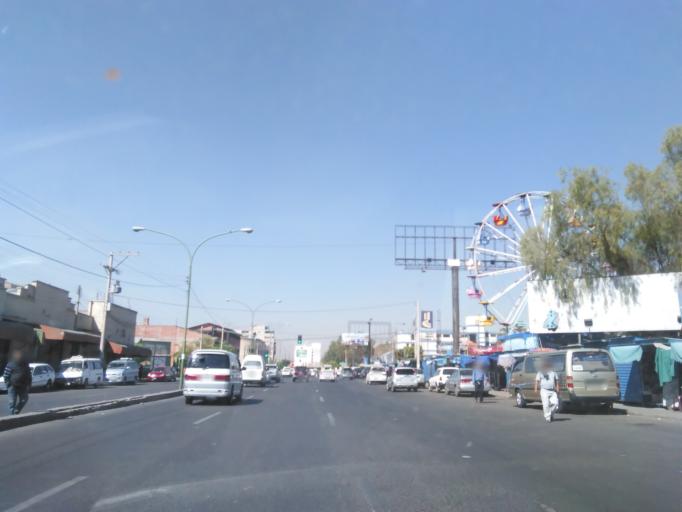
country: BO
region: Cochabamba
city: Cochabamba
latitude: -17.4003
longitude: -66.1577
